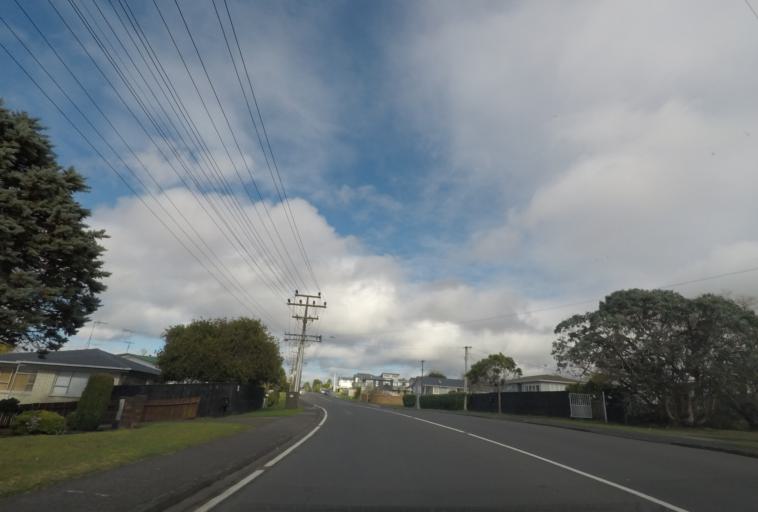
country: NZ
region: Auckland
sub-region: Auckland
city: Waitakere
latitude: -36.8955
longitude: 174.6511
